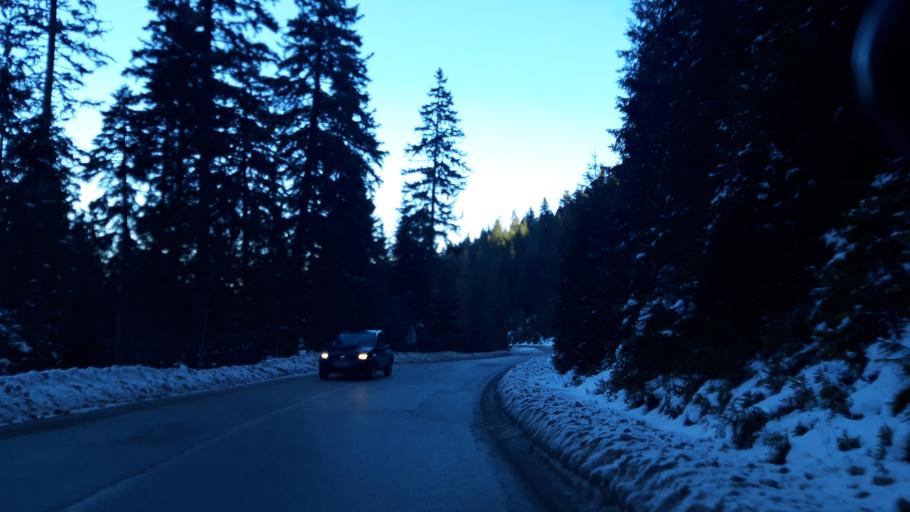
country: BA
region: Republika Srpska
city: Koran
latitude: 43.7679
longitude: 18.5477
